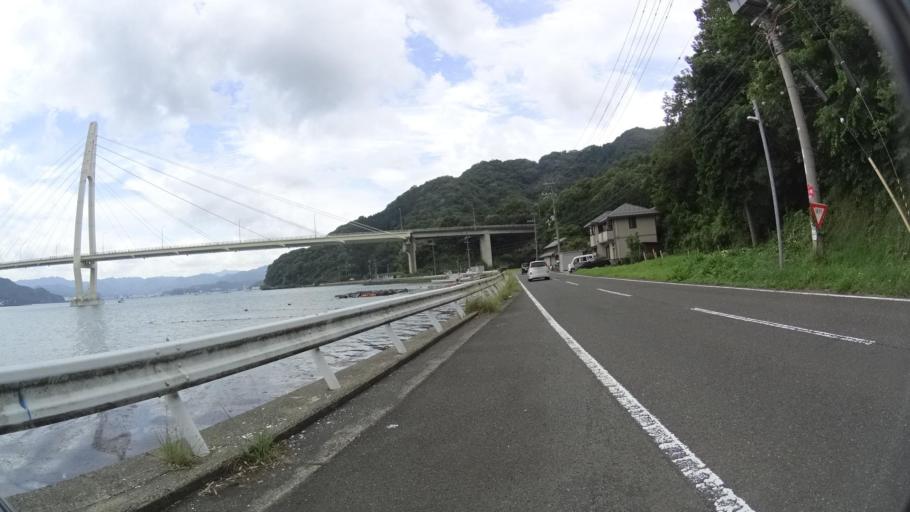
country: JP
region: Kyoto
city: Maizuru
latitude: 35.5122
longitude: 135.3711
